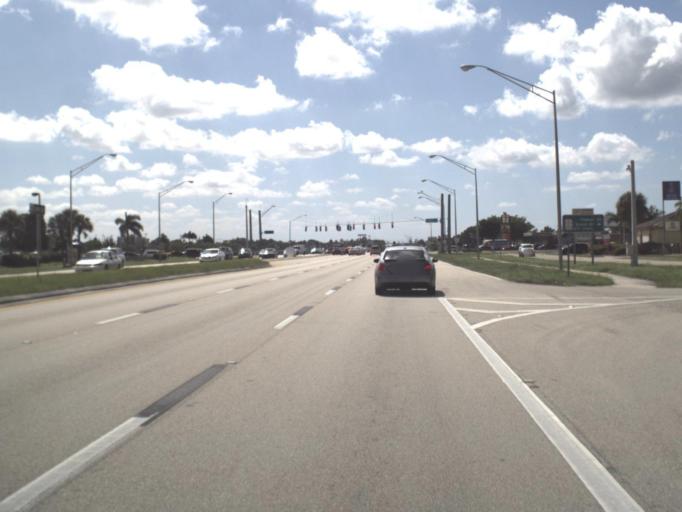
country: US
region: Florida
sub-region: Lee County
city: Pine Manor
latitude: 26.5849
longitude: -81.8720
